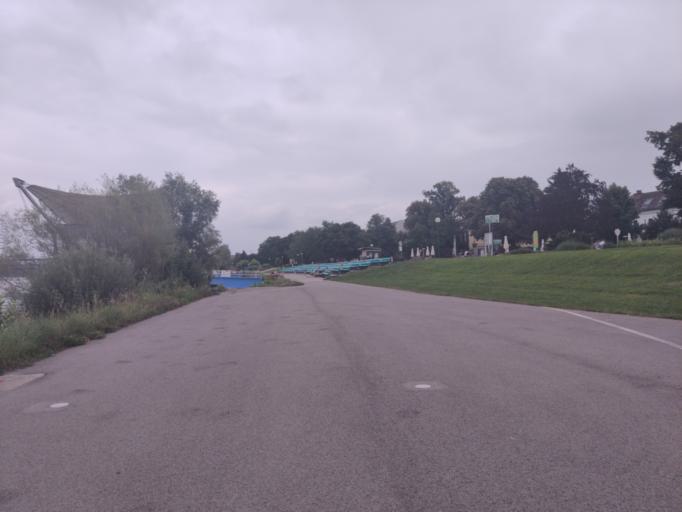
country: AT
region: Lower Austria
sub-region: Politischer Bezirk Tulln
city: Tulln
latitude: 48.3338
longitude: 16.0516
